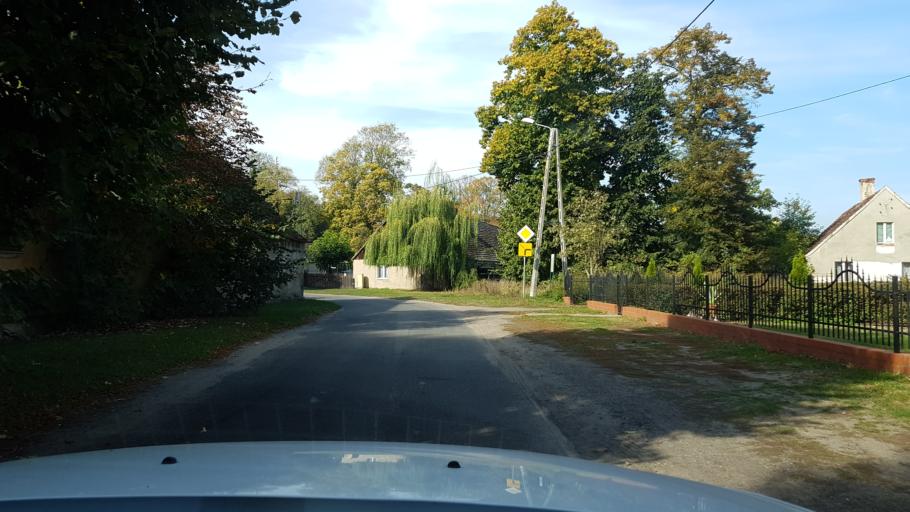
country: PL
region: West Pomeranian Voivodeship
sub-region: Powiat mysliborski
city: Mysliborz
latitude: 52.9311
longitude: 14.9424
